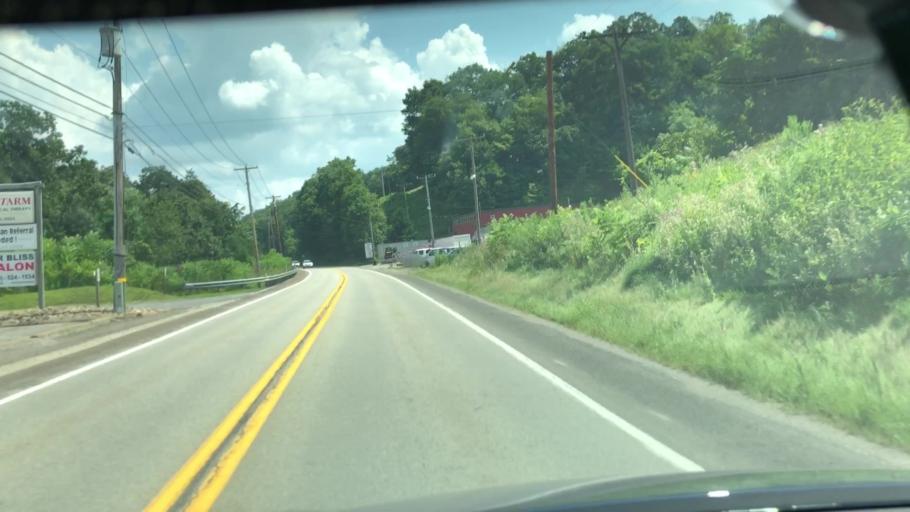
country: US
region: Pennsylvania
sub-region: Armstrong County
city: Freeport
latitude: 40.7126
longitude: -79.7449
